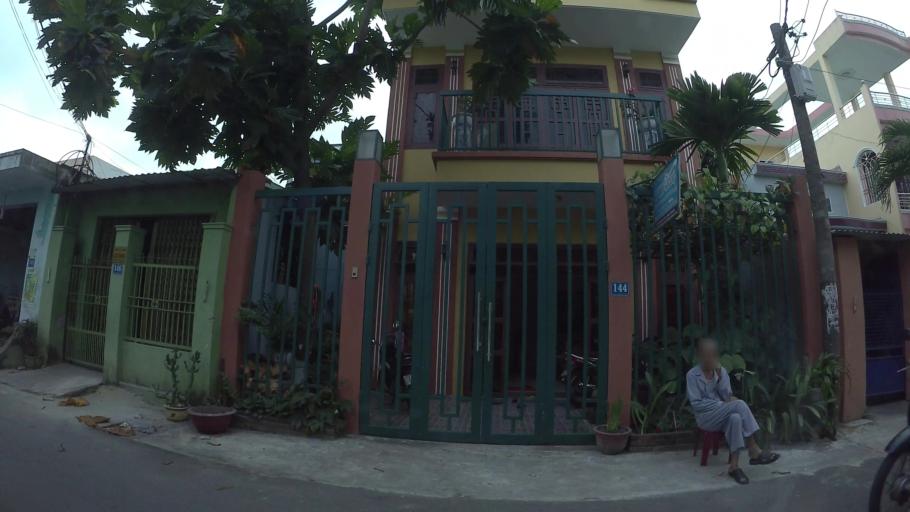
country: VN
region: Da Nang
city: Son Tra
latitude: 16.0561
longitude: 108.2368
